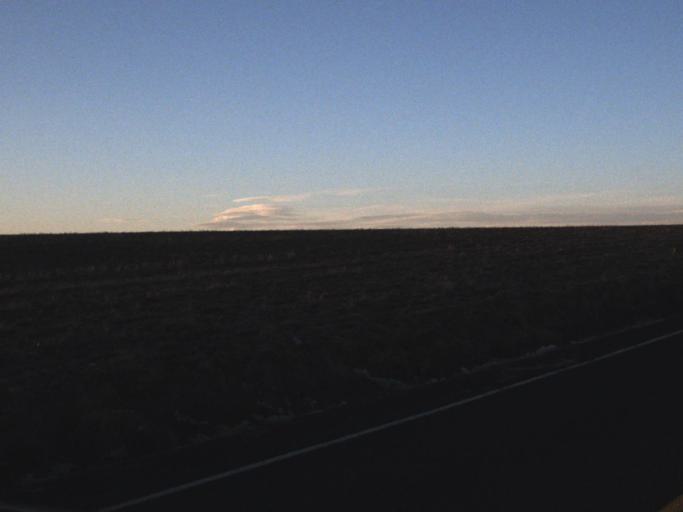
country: US
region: Washington
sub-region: Adams County
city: Ritzville
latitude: 47.0517
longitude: -118.6630
